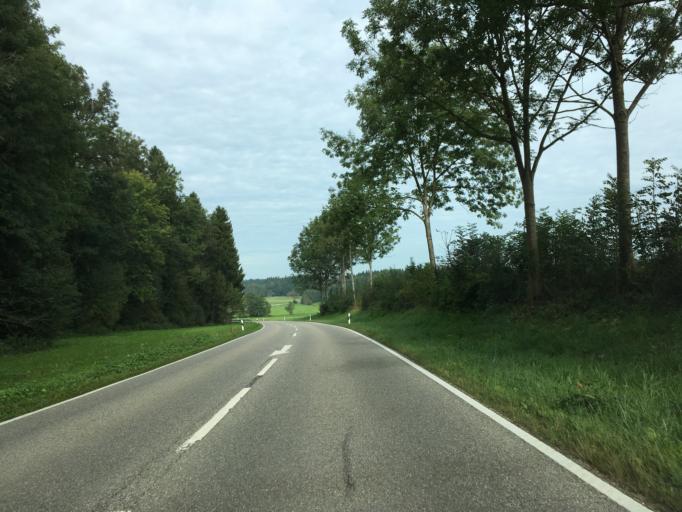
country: DE
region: Bavaria
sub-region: Upper Bavaria
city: Schonstett
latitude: 47.9925
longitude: 12.2608
